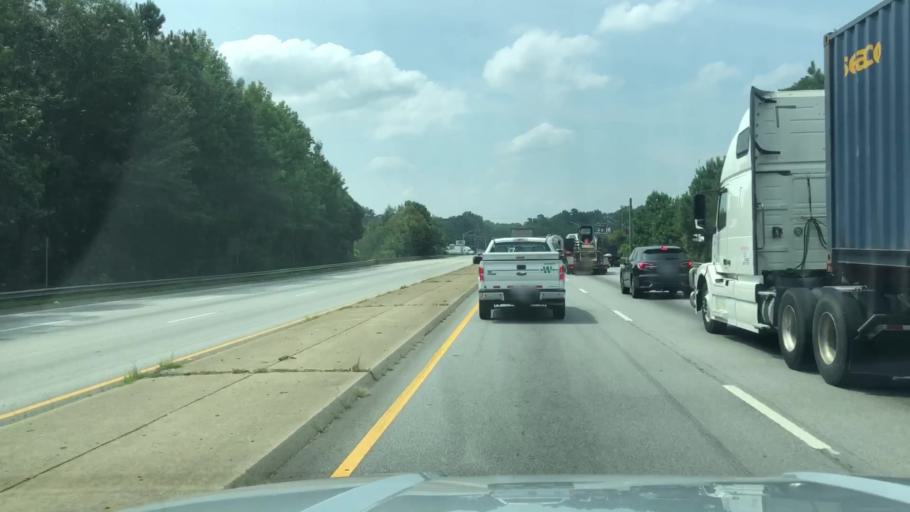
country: US
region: Georgia
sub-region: Cobb County
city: Austell
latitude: 33.7959
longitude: -84.6395
